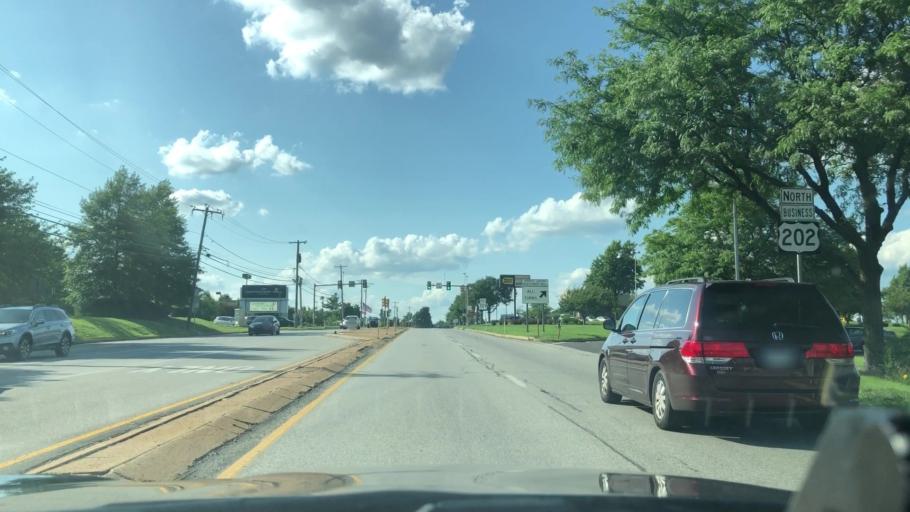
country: US
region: Pennsylvania
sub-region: Montgomery County
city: Montgomeryville
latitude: 40.2355
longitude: -75.2401
